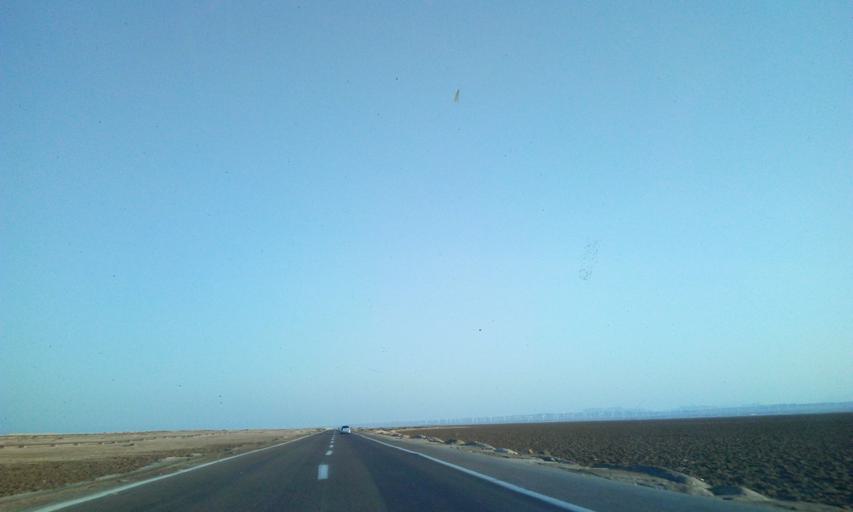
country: EG
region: South Sinai
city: Tor
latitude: 28.2597
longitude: 33.1525
